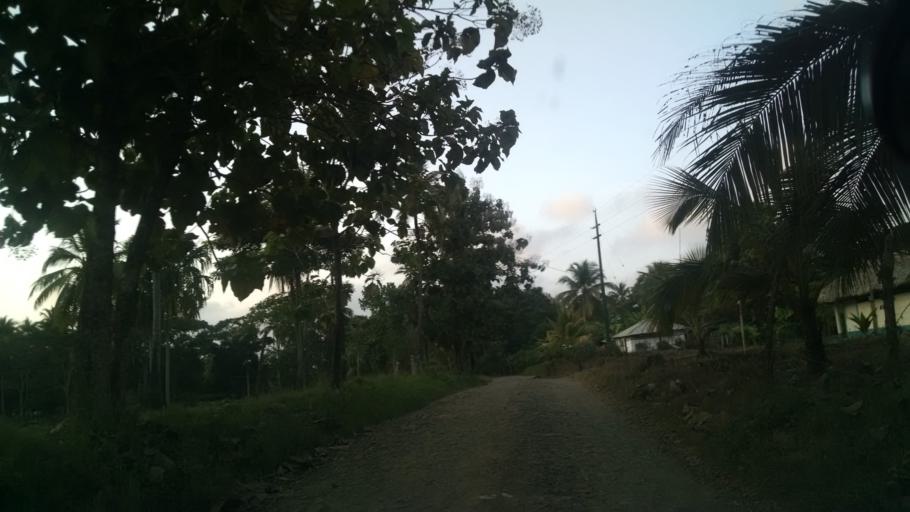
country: CO
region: Antioquia
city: San Juan de Uraba
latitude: 8.7223
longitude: -76.6027
